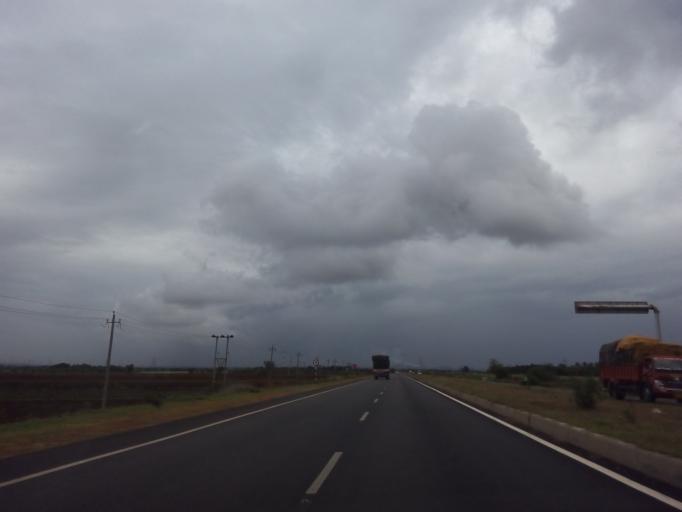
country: IN
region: Karnataka
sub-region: Davanagere
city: Harihar
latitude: 14.5496
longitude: 75.7405
